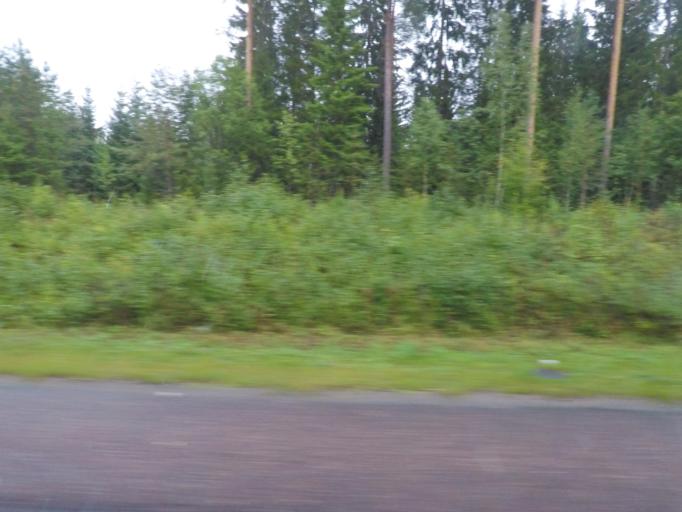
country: FI
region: Northern Savo
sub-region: Varkaus
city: Leppaevirta
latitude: 62.4538
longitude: 27.7875
